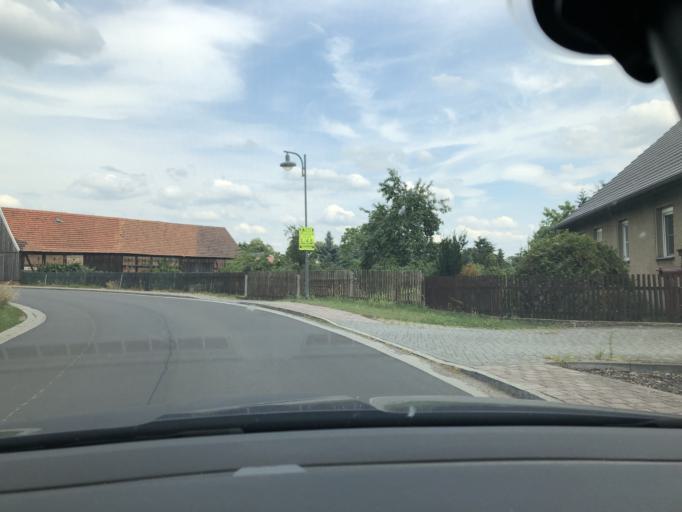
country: DE
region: Brandenburg
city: Schlepzig
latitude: 52.0309
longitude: 13.8287
